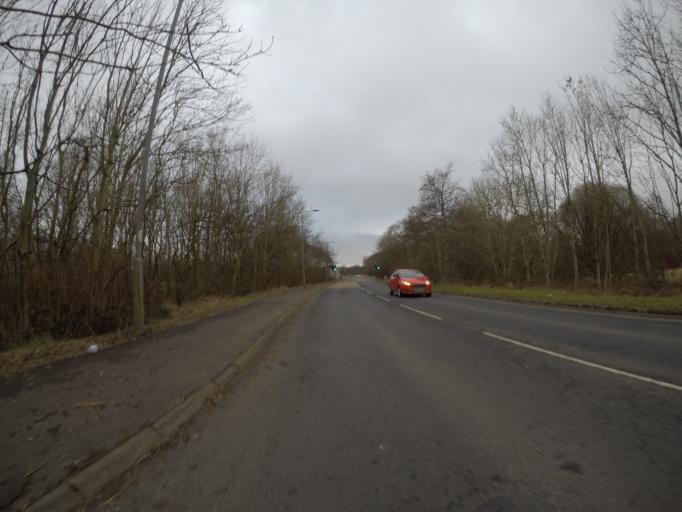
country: GB
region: Scotland
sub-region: North Ayrshire
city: Irvine
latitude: 55.6313
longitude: -4.6423
